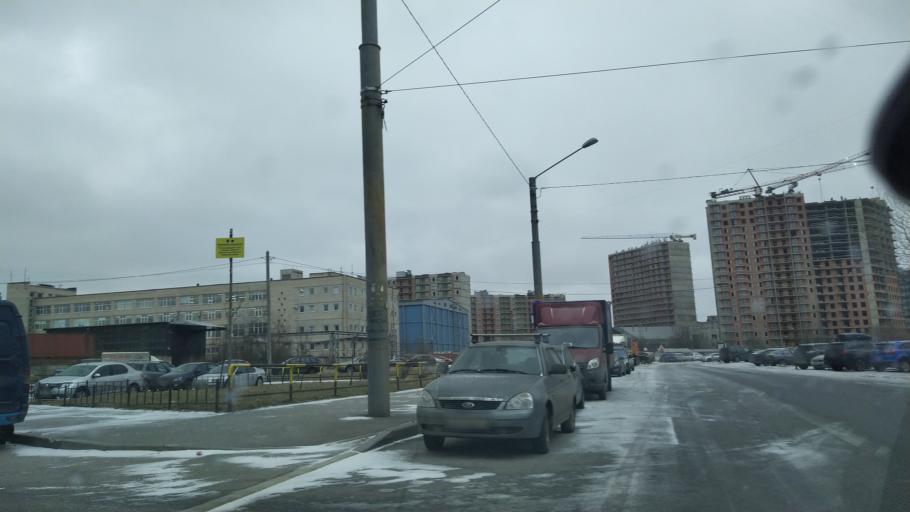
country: RU
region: St.-Petersburg
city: Kupchino
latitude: 59.8415
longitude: 30.3091
